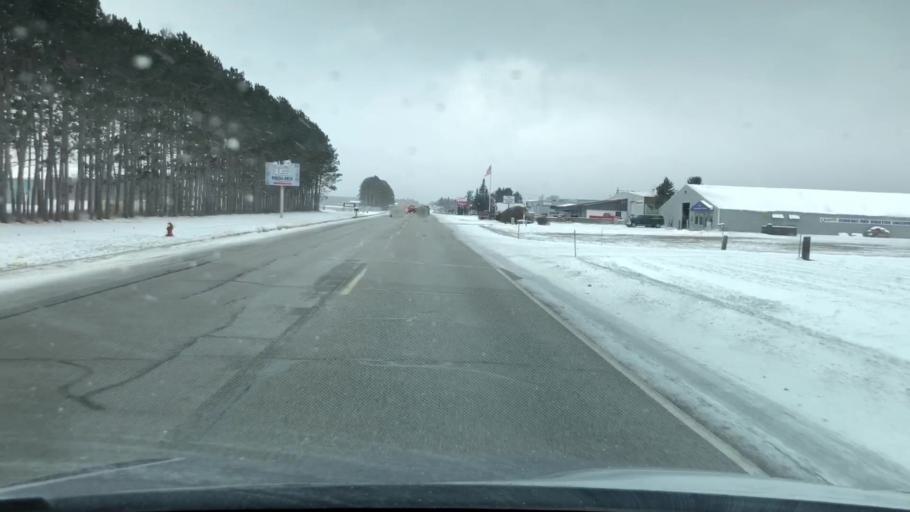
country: US
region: Michigan
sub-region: Wexford County
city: Cadillac
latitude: 44.2813
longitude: -85.4143
